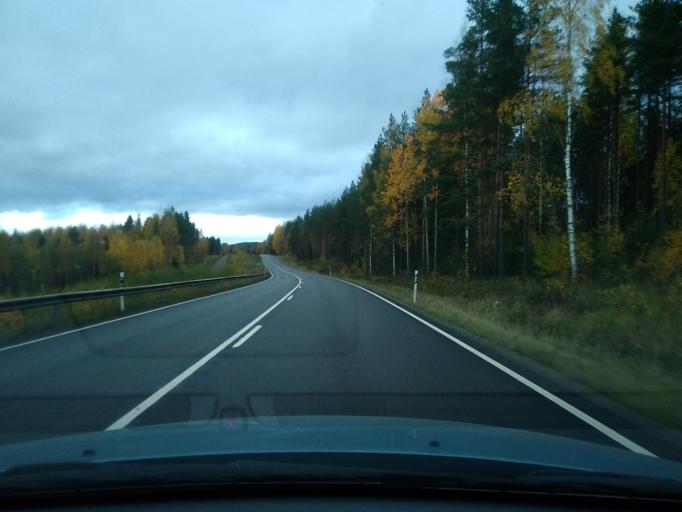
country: FI
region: Central Finland
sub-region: Jyvaeskylae
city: Uurainen
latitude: 62.6259
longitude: 25.5376
